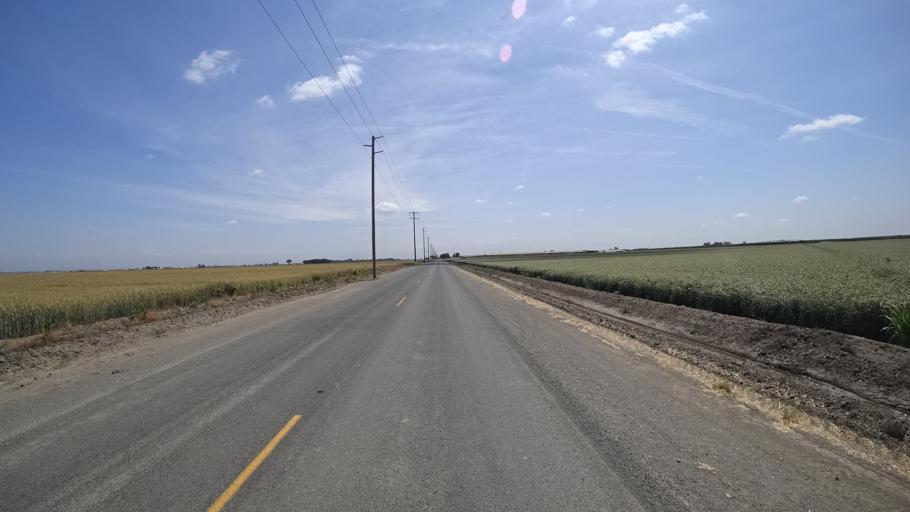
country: US
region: California
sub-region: Tulare County
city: Goshen
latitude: 36.2833
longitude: -119.4905
